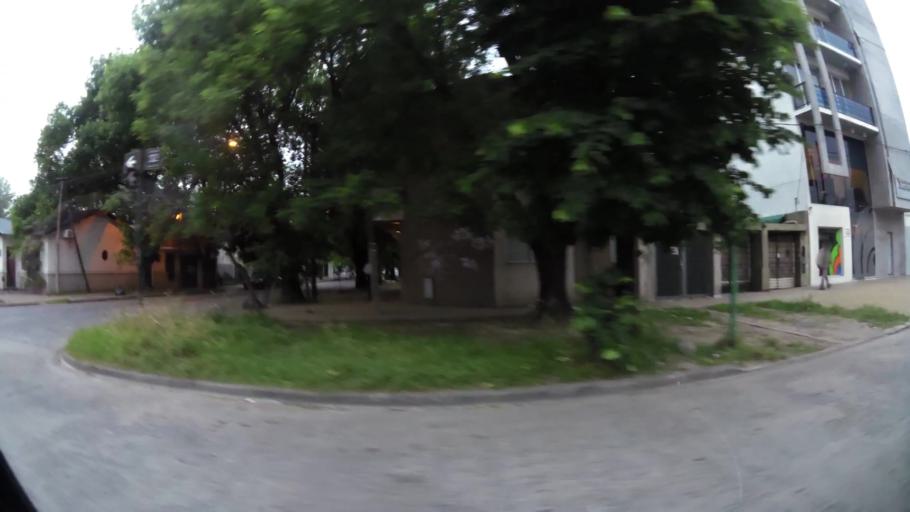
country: AR
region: Buenos Aires
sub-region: Partido de La Plata
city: La Plata
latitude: -34.9109
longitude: -57.9802
